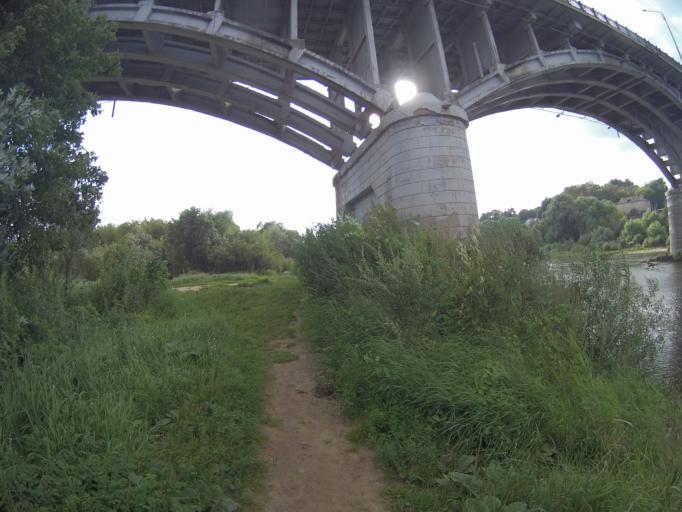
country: RU
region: Vladimir
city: Vladimir
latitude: 56.1227
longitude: 40.4098
